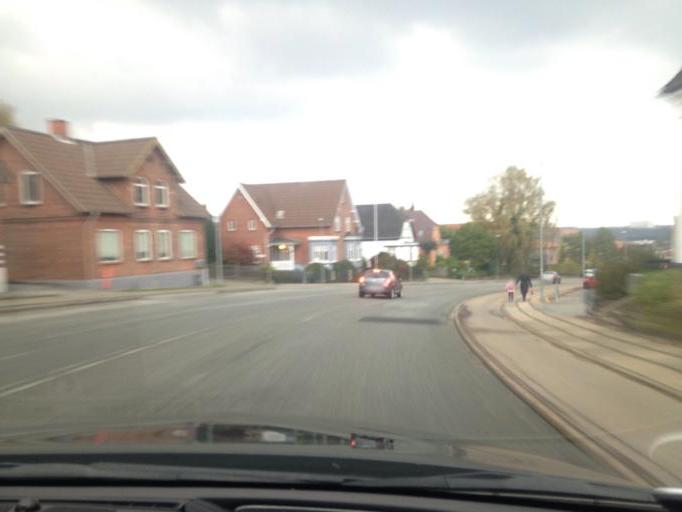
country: DK
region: South Denmark
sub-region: Kolding Kommune
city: Kolding
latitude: 55.4811
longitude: 9.4684
